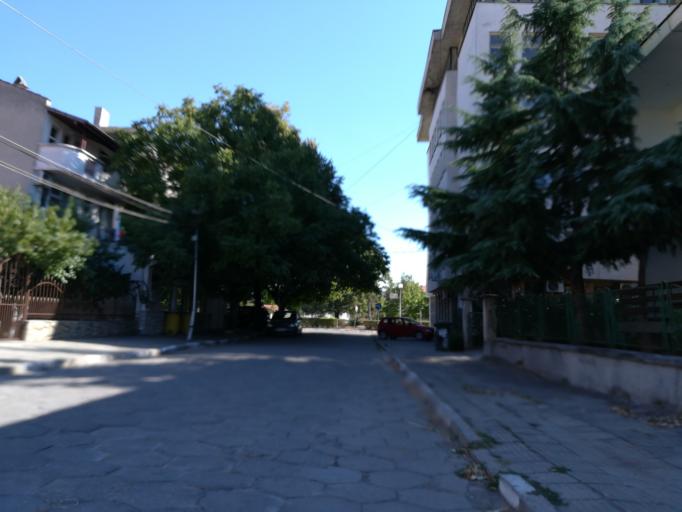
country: BG
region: Stara Zagora
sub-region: Obshtina Chirpan
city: Chirpan
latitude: 42.0999
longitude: 25.2281
